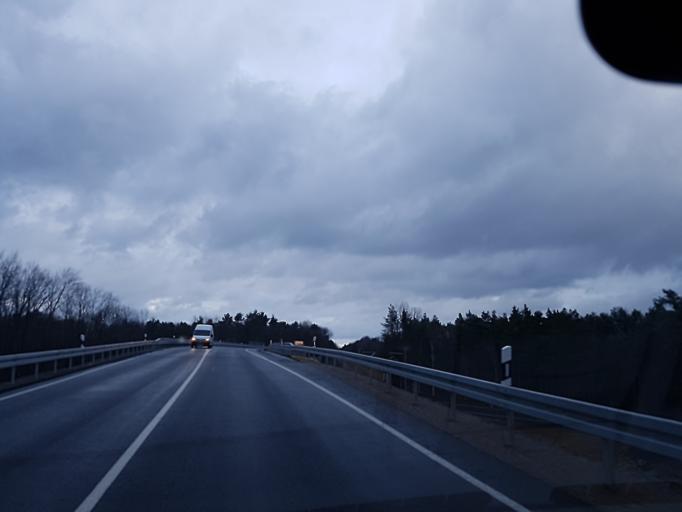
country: DE
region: Brandenburg
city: Hohenleipisch
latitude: 51.5213
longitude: 13.5752
